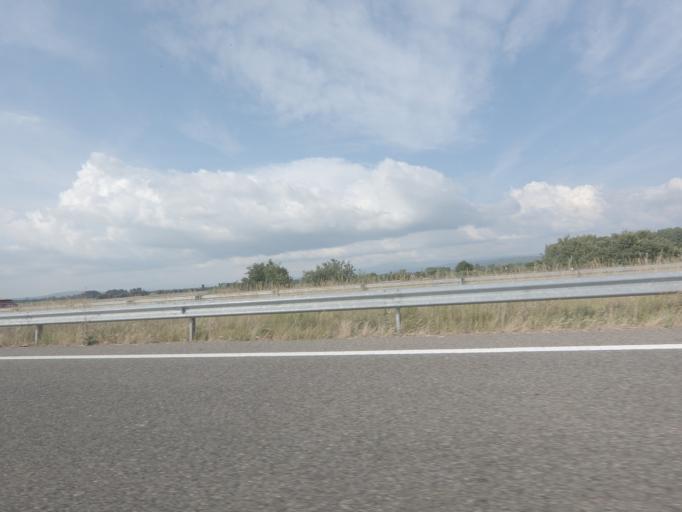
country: ES
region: Galicia
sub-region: Provincia de Ourense
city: Xinzo de Limia
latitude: 42.0871
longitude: -7.7200
